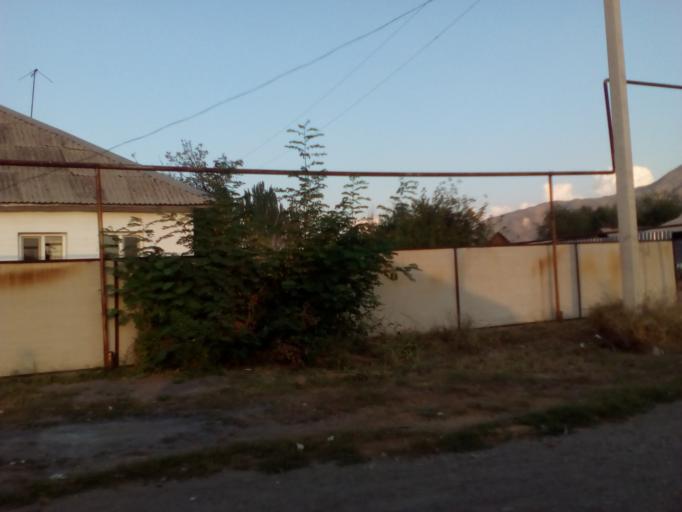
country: KZ
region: Almaty Oblysy
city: Burunday
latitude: 43.1663
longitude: 76.4011
